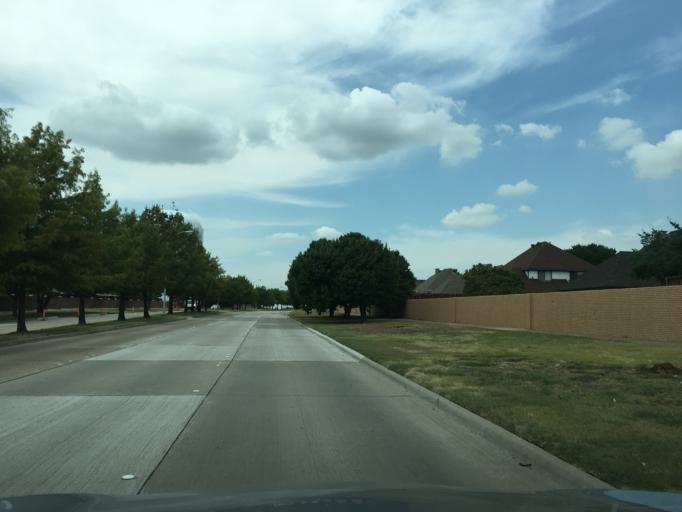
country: US
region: Texas
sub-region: Collin County
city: Plano
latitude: 33.0563
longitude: -96.7613
